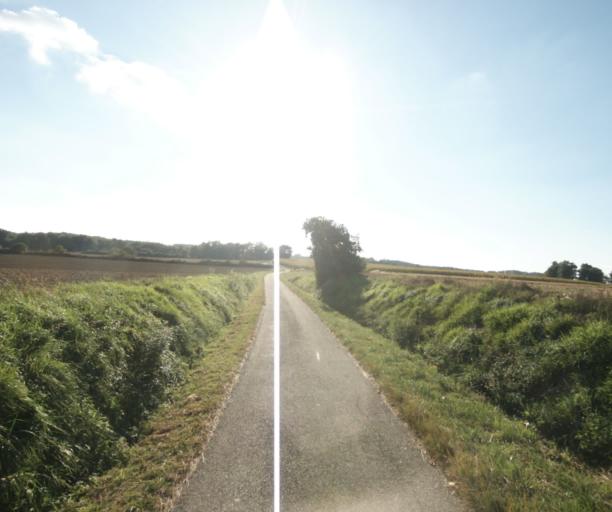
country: FR
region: Midi-Pyrenees
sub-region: Departement du Gers
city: Eauze
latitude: 43.7856
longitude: 0.1433
